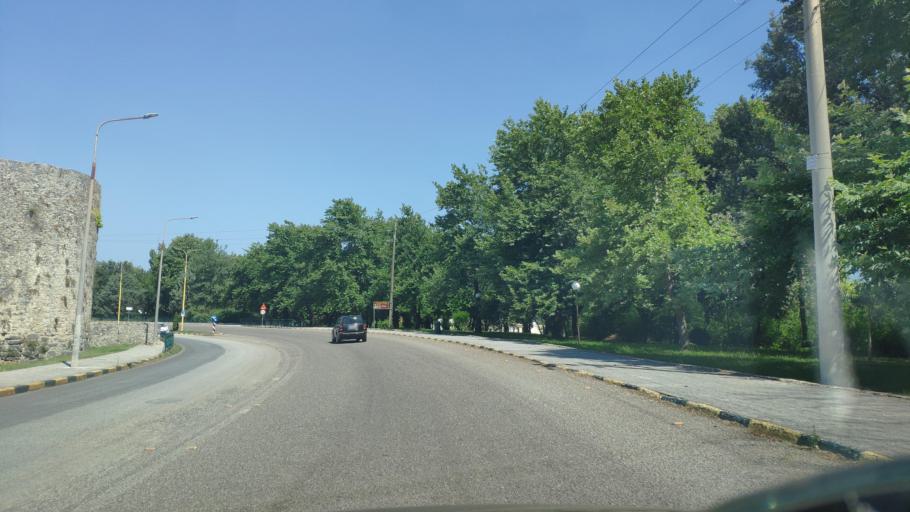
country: GR
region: Epirus
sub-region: Nomos Artas
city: Arta
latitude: 39.1665
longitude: 20.9887
